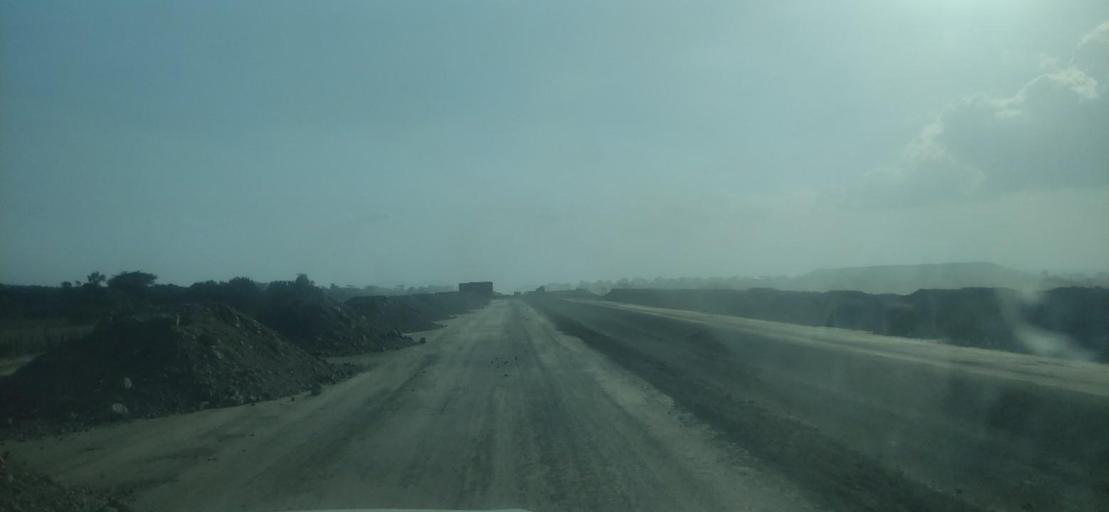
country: ET
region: Southern Nations, Nationalities, and People's Region
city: Hawassa
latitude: 7.1681
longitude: 38.4874
